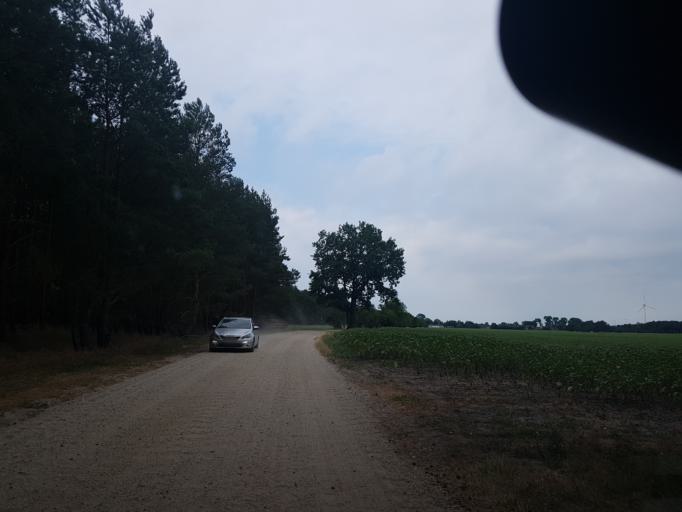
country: DE
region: Brandenburg
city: Schonewalde
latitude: 51.6996
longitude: 13.5258
